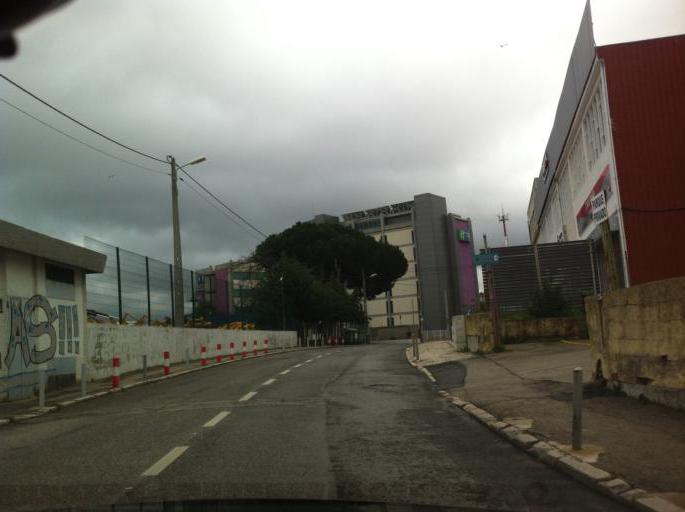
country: PT
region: Lisbon
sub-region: Loures
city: Sacavem
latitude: 38.7871
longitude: -9.1201
